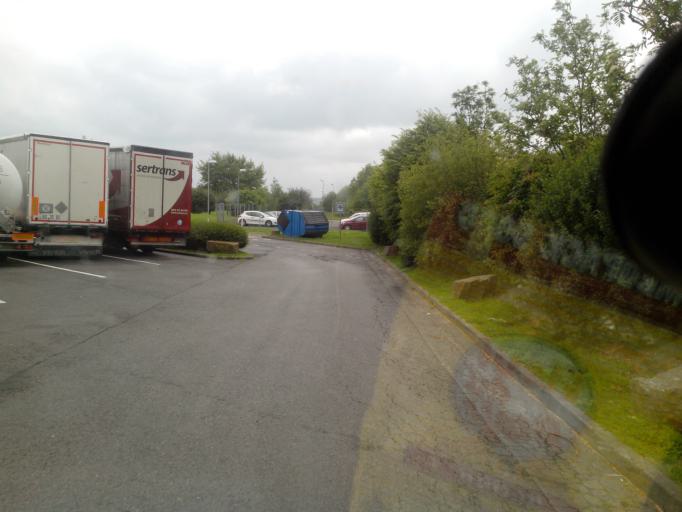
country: FR
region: Lower Normandy
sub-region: Departement de la Manche
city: Tessy-sur-Vire
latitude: 48.9083
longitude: -1.1052
